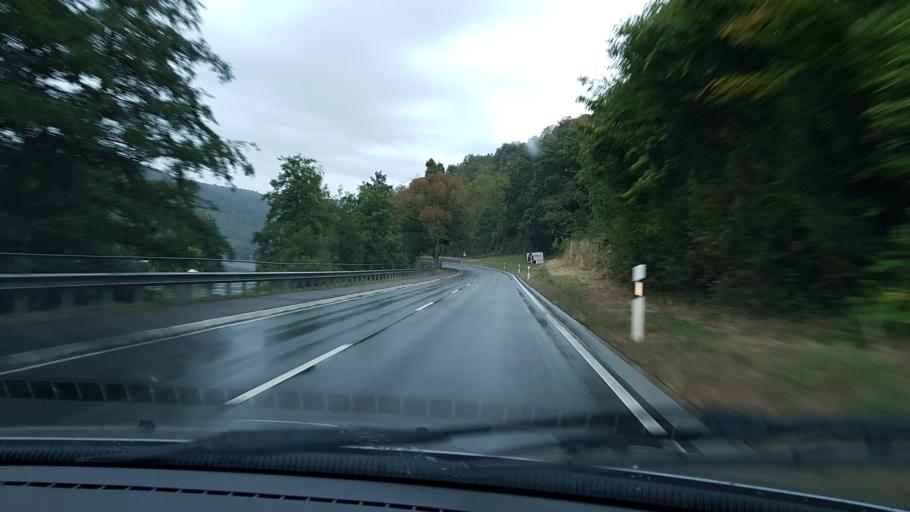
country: DE
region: Rheinland-Pfalz
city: Dausenau
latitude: 50.3278
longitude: 7.7526
